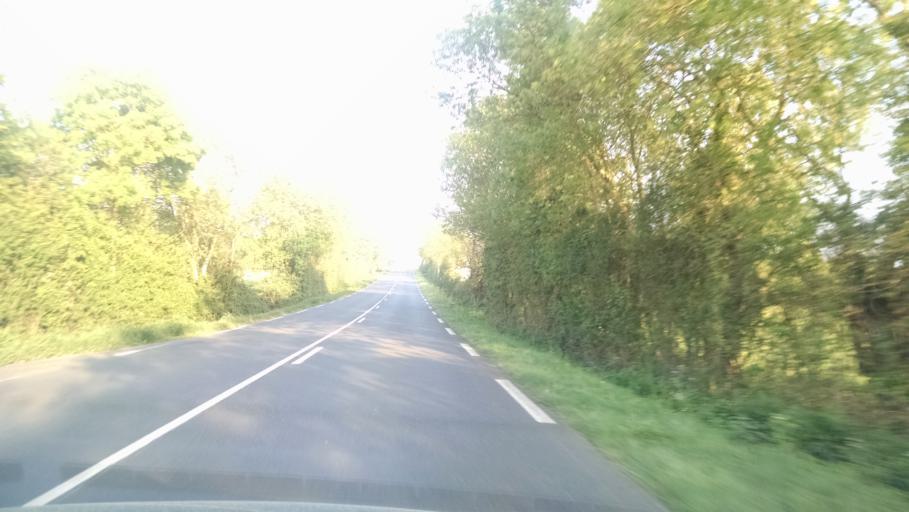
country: FR
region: Pays de la Loire
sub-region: Departement de la Loire-Atlantique
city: Boussay
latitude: 47.0657
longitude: -1.2020
